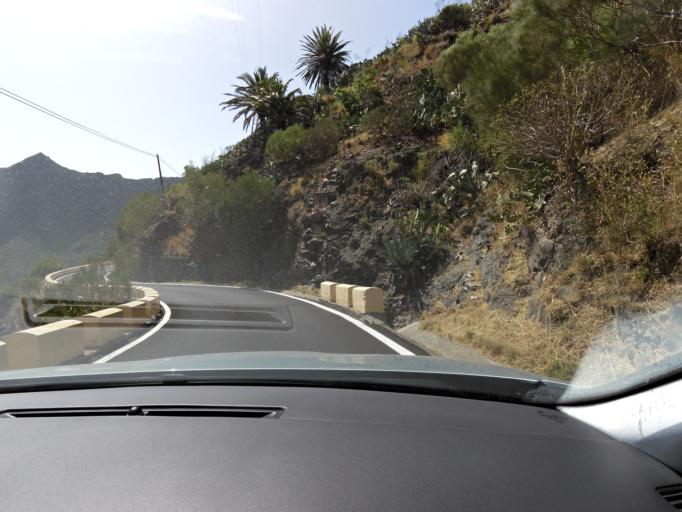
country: ES
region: Canary Islands
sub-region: Provincia de Santa Cruz de Tenerife
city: Santiago del Teide
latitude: 28.3040
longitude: -16.8371
